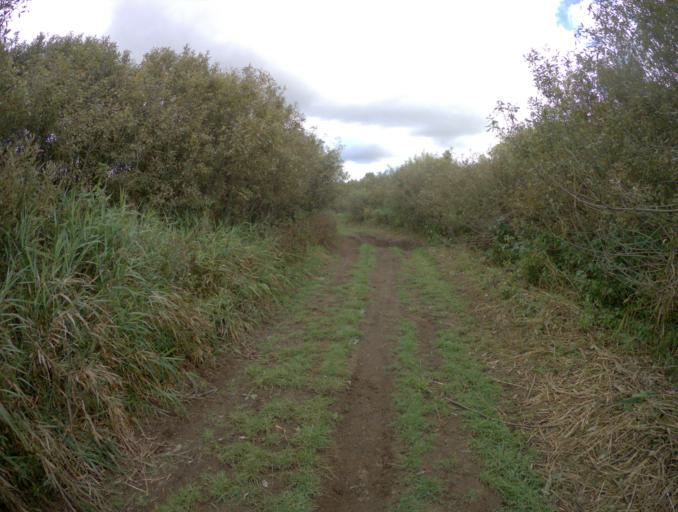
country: RU
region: Moskovskaya
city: Baksheyevo
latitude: 55.7152
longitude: 39.8544
